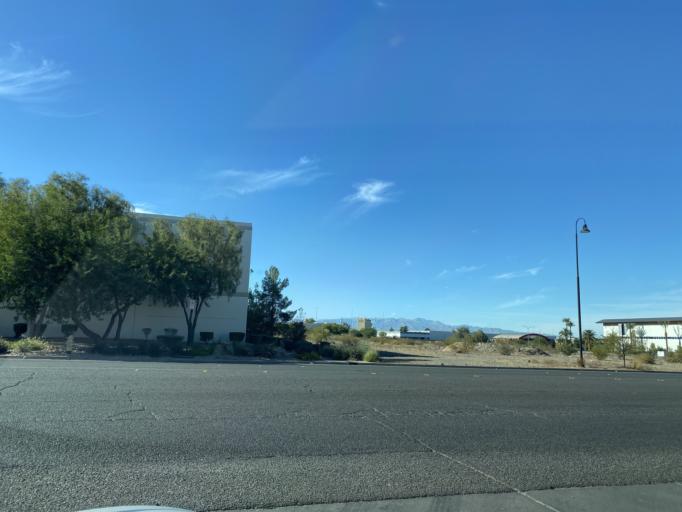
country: US
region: Nevada
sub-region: Clark County
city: Henderson
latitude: 36.0551
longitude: -115.0198
